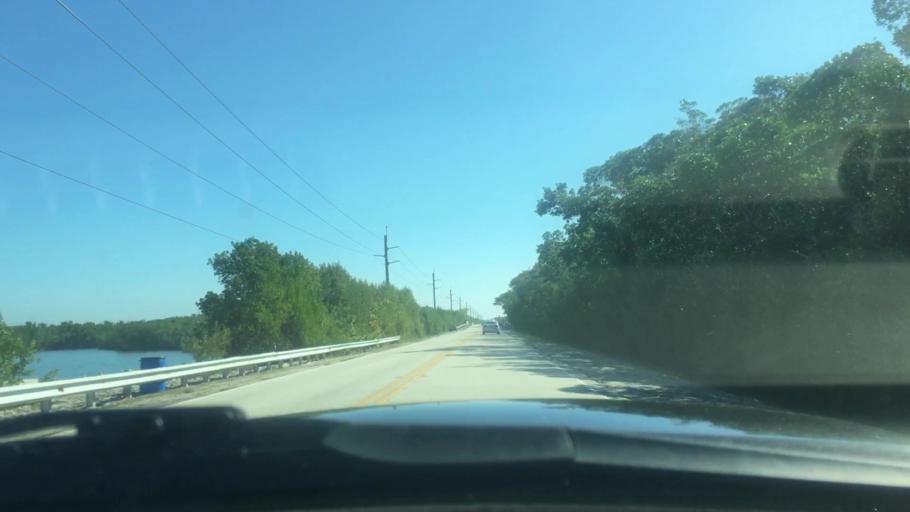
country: US
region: Florida
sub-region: Monroe County
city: North Key Largo
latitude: 25.2835
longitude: -80.3571
